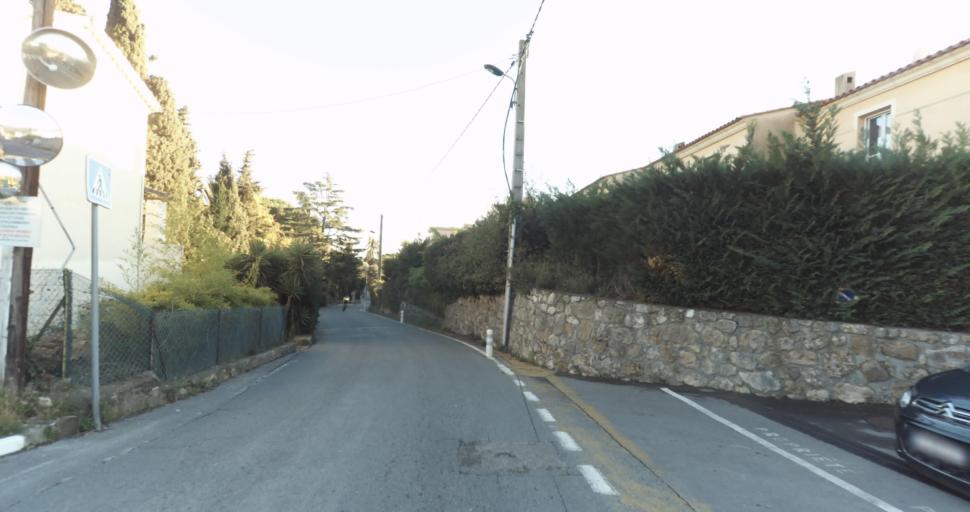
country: FR
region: Provence-Alpes-Cote d'Azur
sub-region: Departement des Alpes-Maritimes
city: Vence
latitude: 43.7270
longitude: 7.1038
